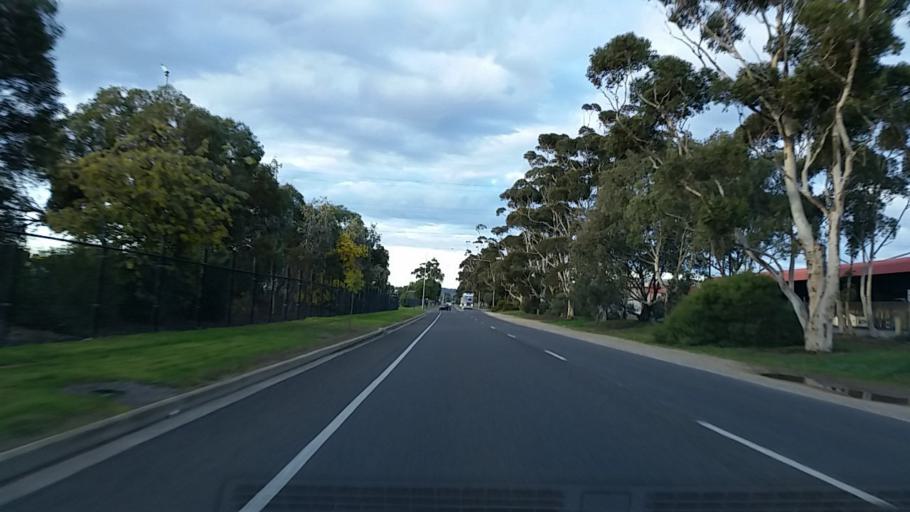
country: AU
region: South Australia
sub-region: Port Adelaide Enfield
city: Enfield
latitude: -34.8292
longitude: 138.6074
